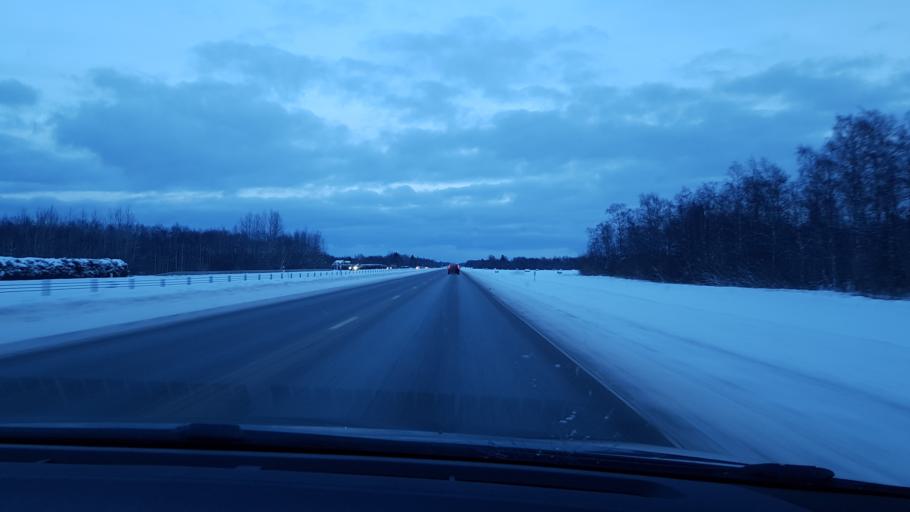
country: EE
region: Harju
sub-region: Anija vald
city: Kehra
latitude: 59.4420
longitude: 25.3191
